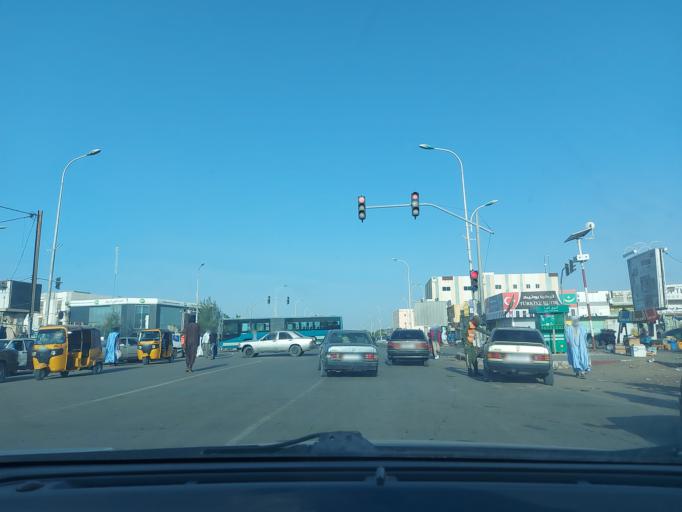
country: MR
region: Nouakchott
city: Nouakchott
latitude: 18.0879
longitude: -15.9799
